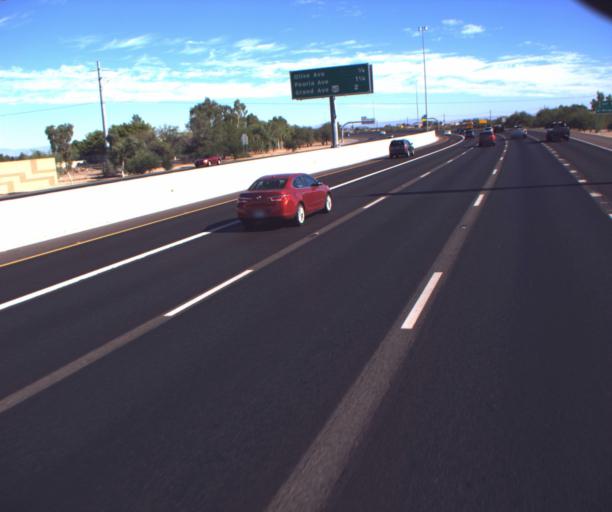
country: US
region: Arizona
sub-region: Maricopa County
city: Peoria
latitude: 33.5579
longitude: -112.2595
